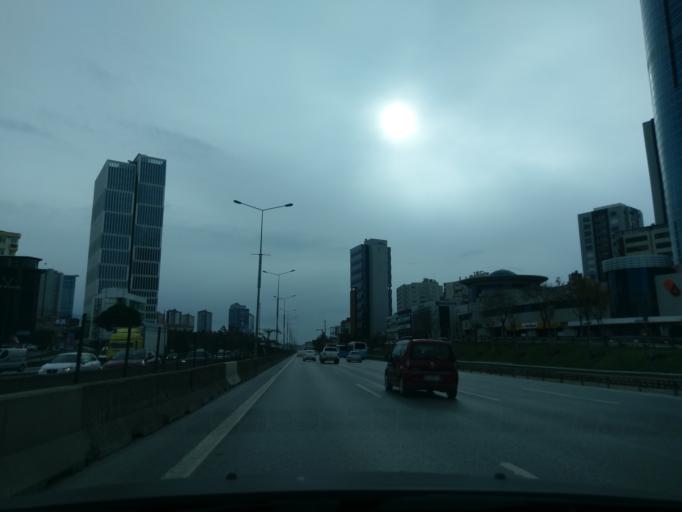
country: TR
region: Istanbul
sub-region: Atasehir
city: Atasehir
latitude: 40.9750
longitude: 29.0991
